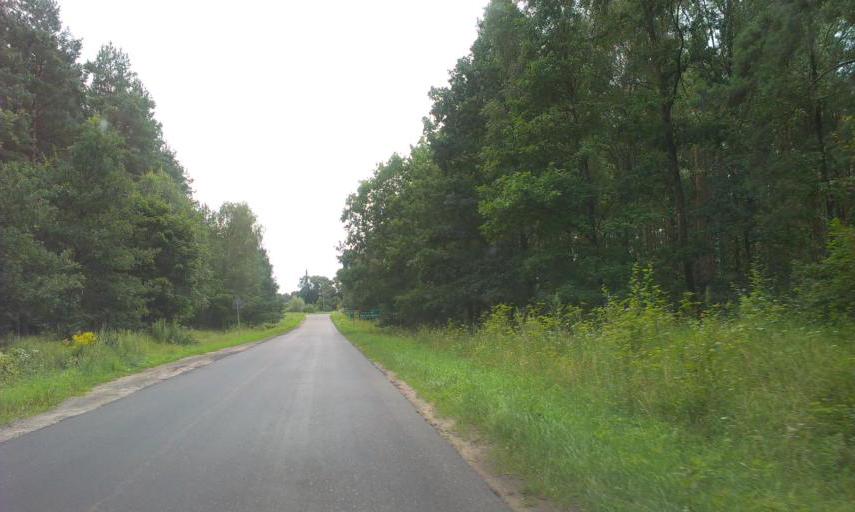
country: PL
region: West Pomeranian Voivodeship
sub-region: Powiat swidwinski
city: Polczyn-Zdroj
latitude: 53.7730
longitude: 16.1508
